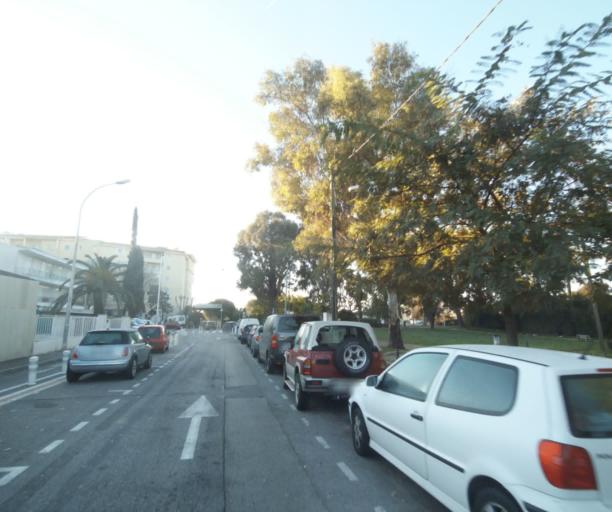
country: FR
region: Provence-Alpes-Cote d'Azur
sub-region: Departement des Alpes-Maritimes
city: Vallauris
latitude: 43.5740
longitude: 7.0871
